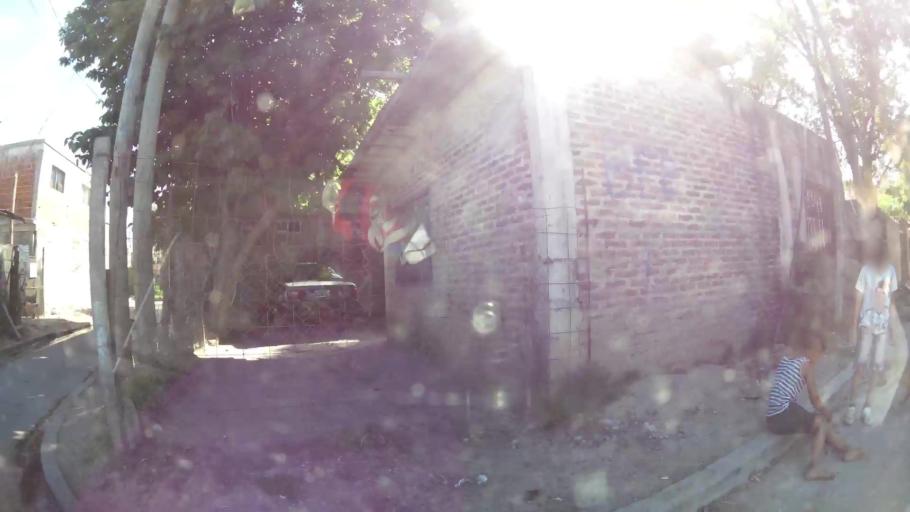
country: AR
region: Buenos Aires
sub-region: Partido de General San Martin
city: General San Martin
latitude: -34.5231
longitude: -58.5807
